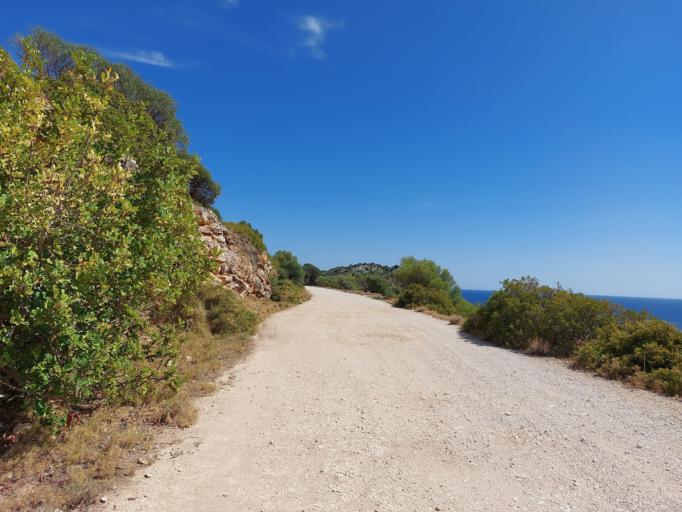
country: HR
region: Dubrovacko-Neretvanska
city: Smokvica
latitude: 42.7338
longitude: 16.8367
